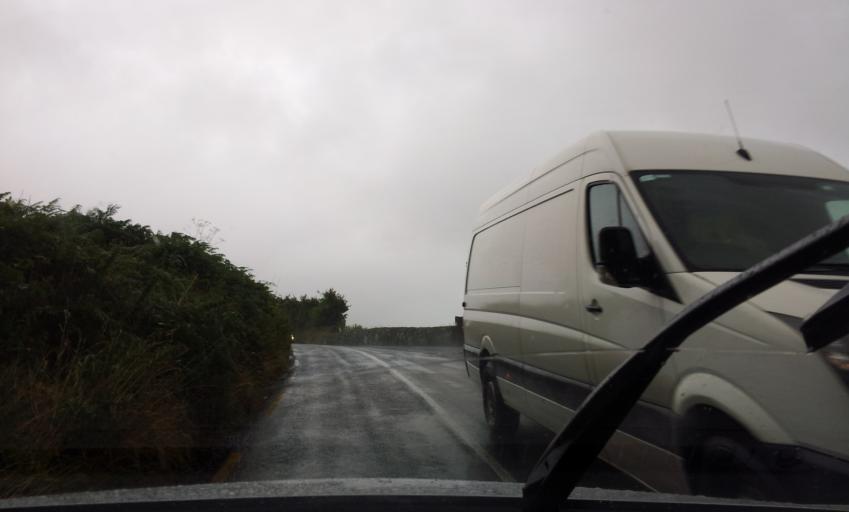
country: IE
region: Leinster
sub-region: Loch Garman
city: New Ross
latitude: 52.4080
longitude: -7.0415
